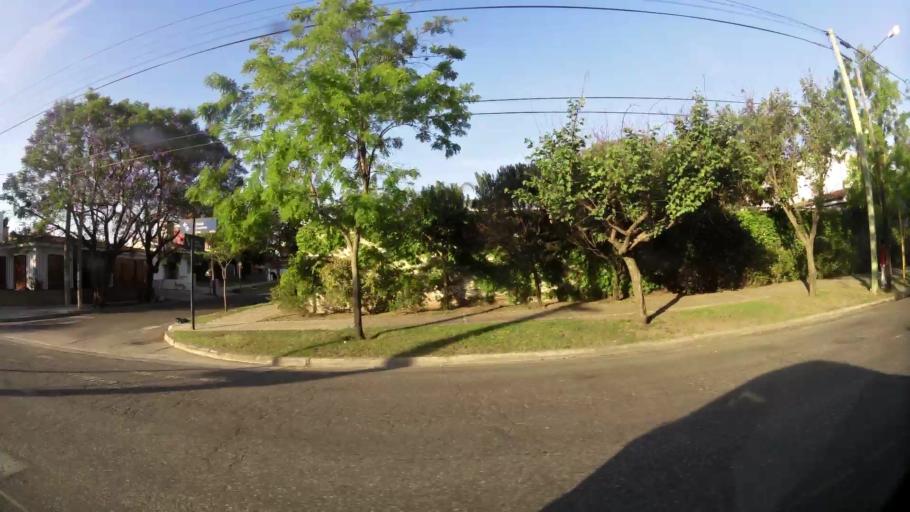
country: AR
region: Cordoba
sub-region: Departamento de Capital
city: Cordoba
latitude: -31.3818
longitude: -64.2439
